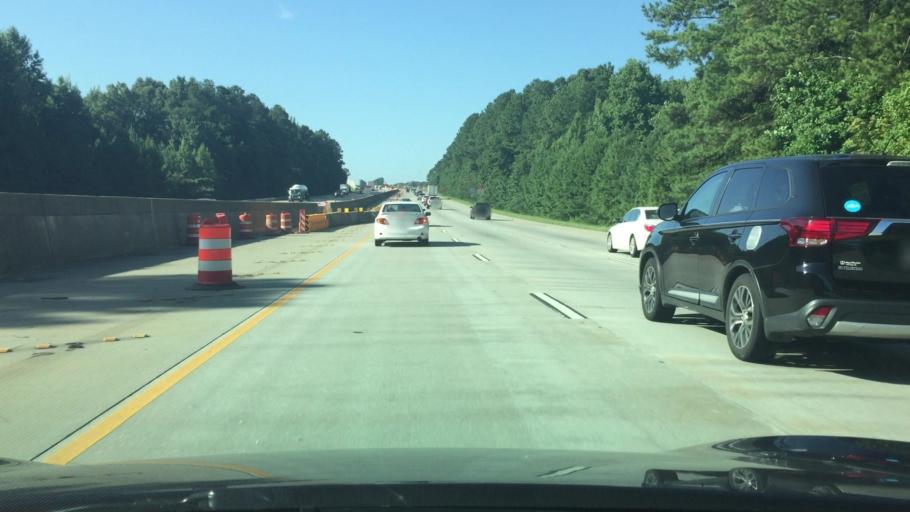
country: US
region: Georgia
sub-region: Coweta County
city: East Newnan
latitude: 33.3735
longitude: -84.7584
